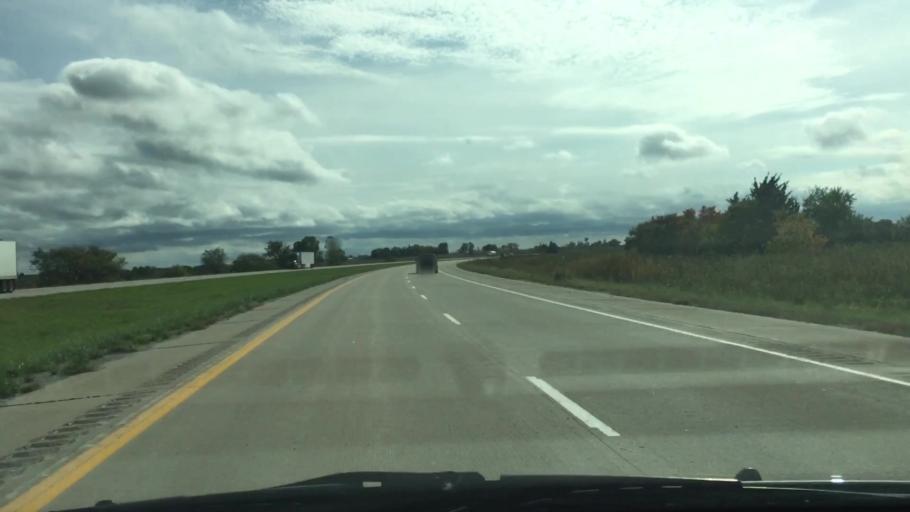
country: US
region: Iowa
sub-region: Decatur County
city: Leon
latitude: 40.8453
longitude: -93.8045
